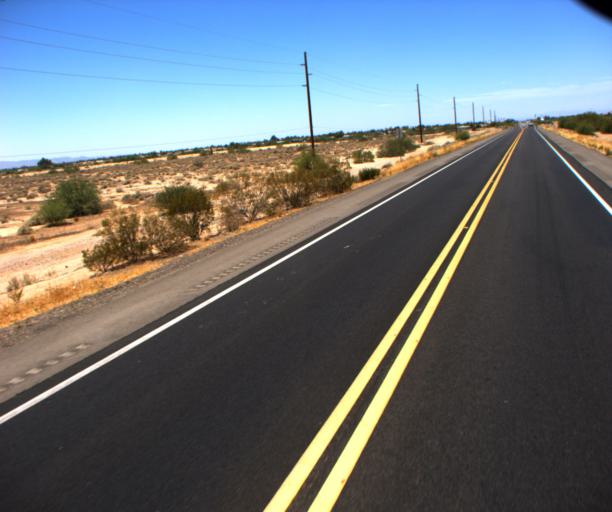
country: US
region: Arizona
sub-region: Maricopa County
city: Sun Lakes
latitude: 33.1893
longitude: -111.8409
